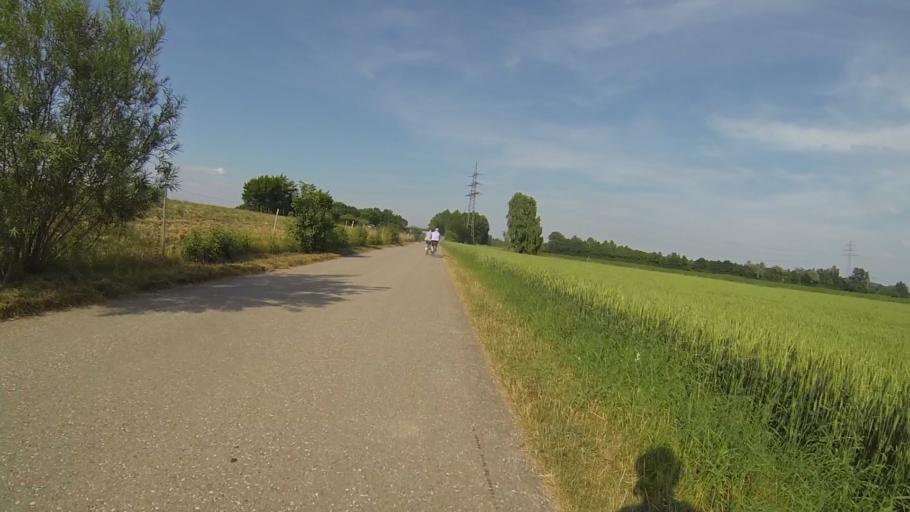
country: DE
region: Bavaria
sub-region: Swabia
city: Neu-Ulm
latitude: 48.3903
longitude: 10.0492
